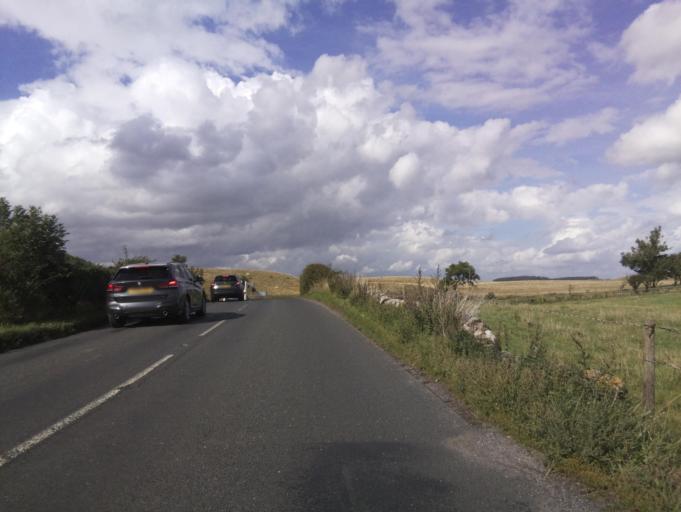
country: GB
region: England
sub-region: North Yorkshire
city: Leyburn
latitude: 54.3421
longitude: -1.8203
